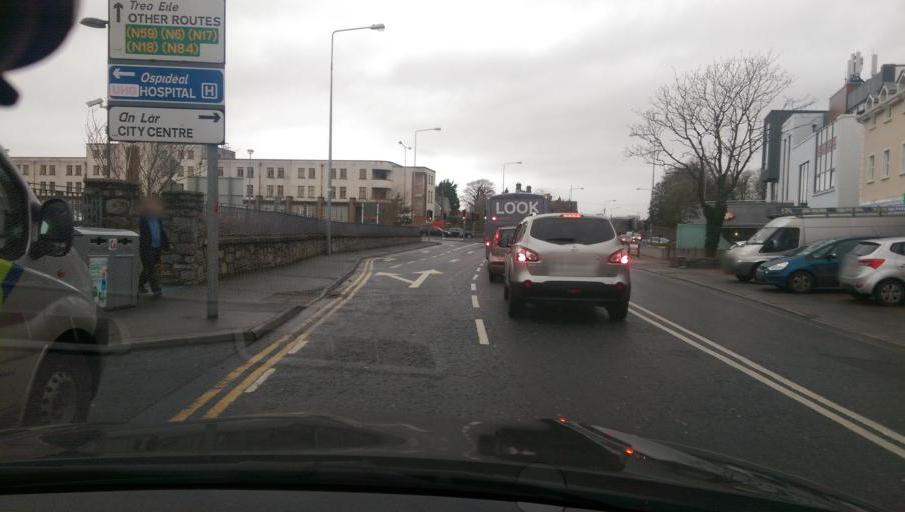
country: IE
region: Connaught
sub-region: County Galway
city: Gaillimh
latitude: 53.2762
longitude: -9.0635
